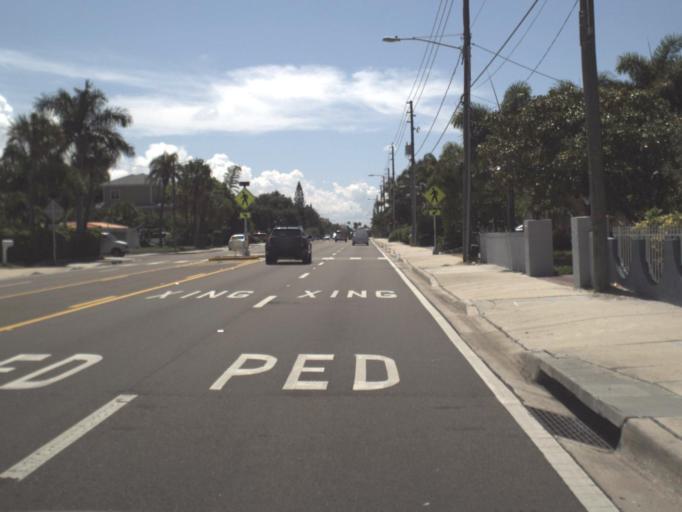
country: US
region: Florida
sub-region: Pinellas County
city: Redington Beach
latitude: 27.8083
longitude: -82.8112
